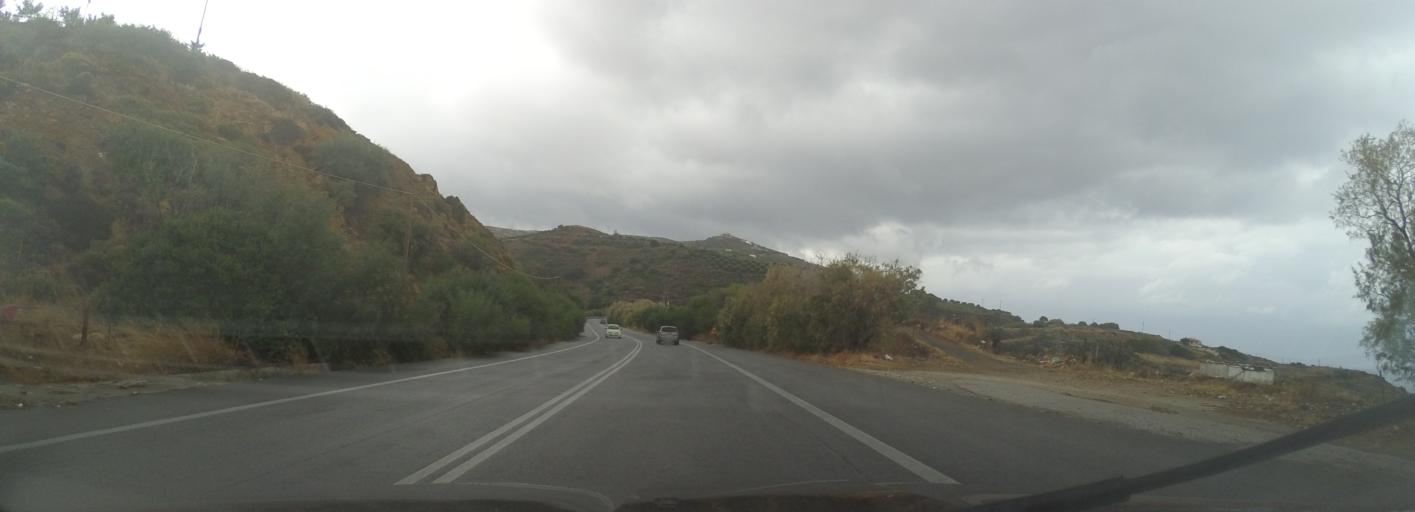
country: GR
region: Crete
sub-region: Nomos Irakleiou
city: Gazi
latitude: 35.3916
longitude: 25.0267
